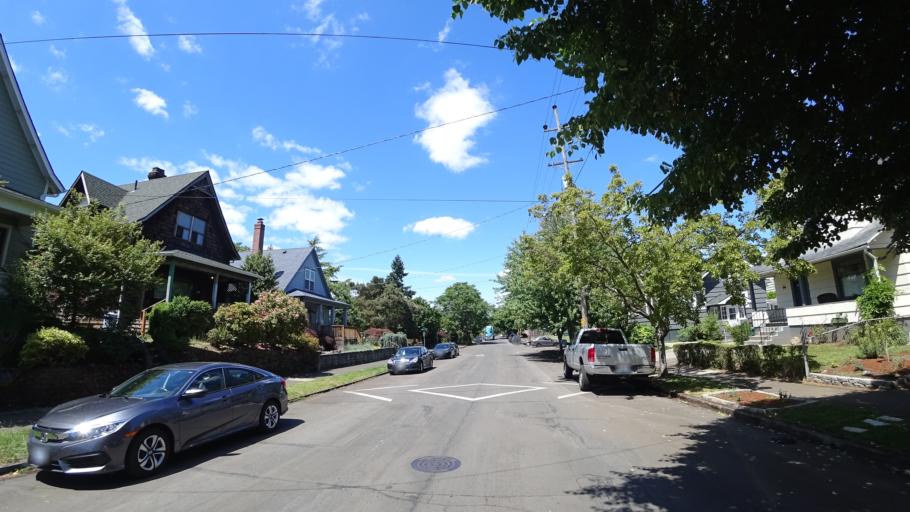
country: US
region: Oregon
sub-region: Multnomah County
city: Portland
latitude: 45.5614
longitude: -122.6848
